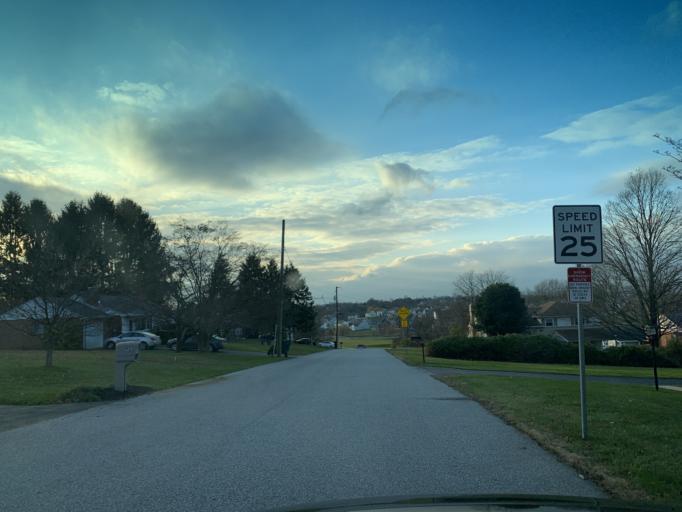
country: US
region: Pennsylvania
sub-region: York County
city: Yoe
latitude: 39.9366
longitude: -76.6443
